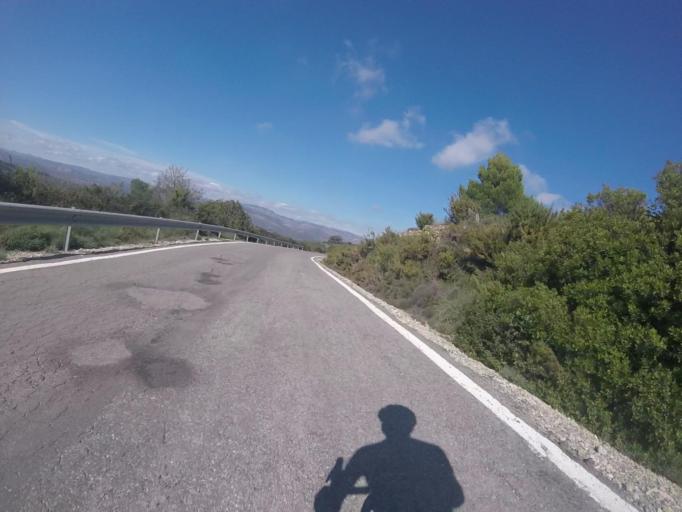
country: ES
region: Valencia
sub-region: Provincia de Castello
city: Albocasser
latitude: 40.3524
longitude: 0.0466
